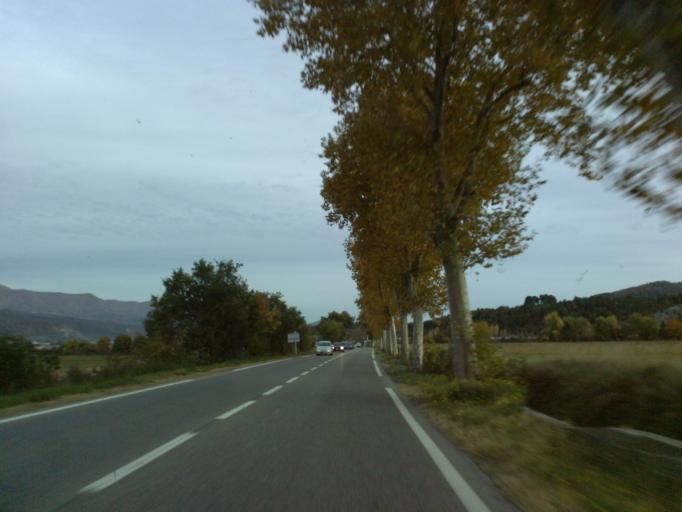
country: FR
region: Provence-Alpes-Cote d'Azur
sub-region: Departement des Alpes-de-Haute-Provence
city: Peipin
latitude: 44.1305
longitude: 5.9754
